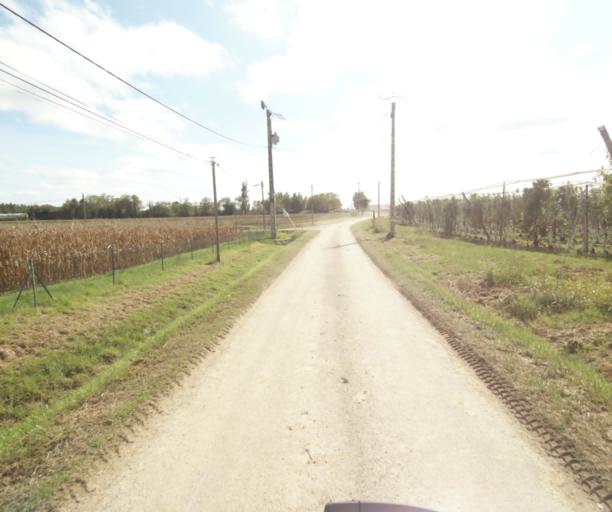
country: FR
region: Midi-Pyrenees
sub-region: Departement du Tarn-et-Garonne
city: Montech
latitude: 43.9412
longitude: 1.2065
